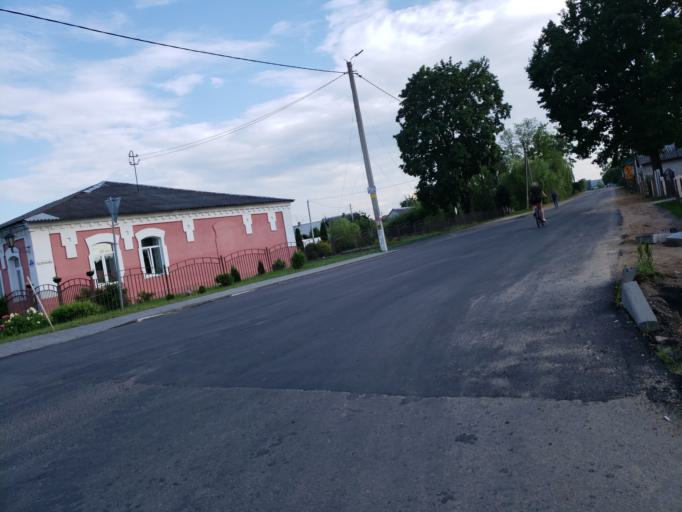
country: BY
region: Minsk
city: Chervyen'
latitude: 53.7080
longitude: 28.4303
